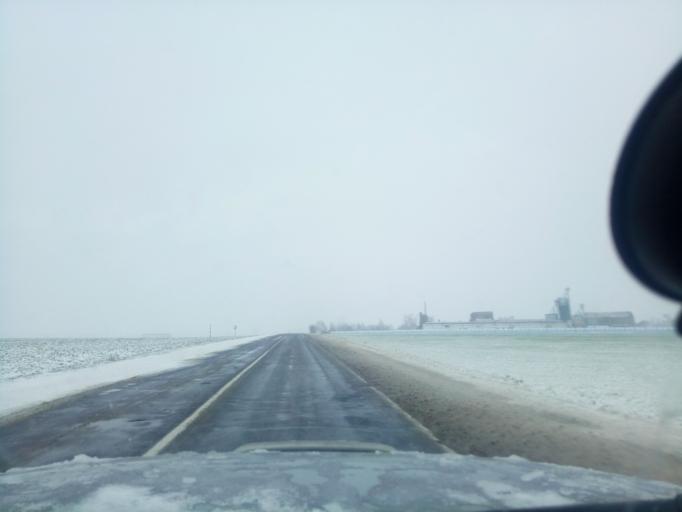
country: BY
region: Minsk
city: Haradzyeya
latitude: 53.3214
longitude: 26.5565
